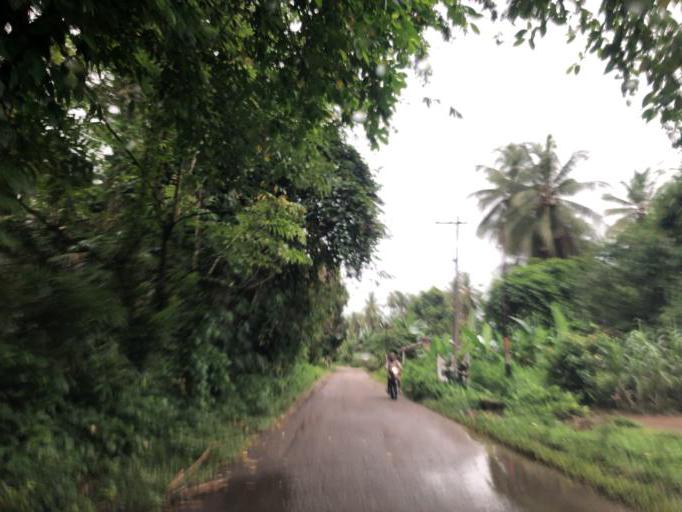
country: ID
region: West Sumatra
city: Pauhambar
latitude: -0.6236
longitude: 100.2136
